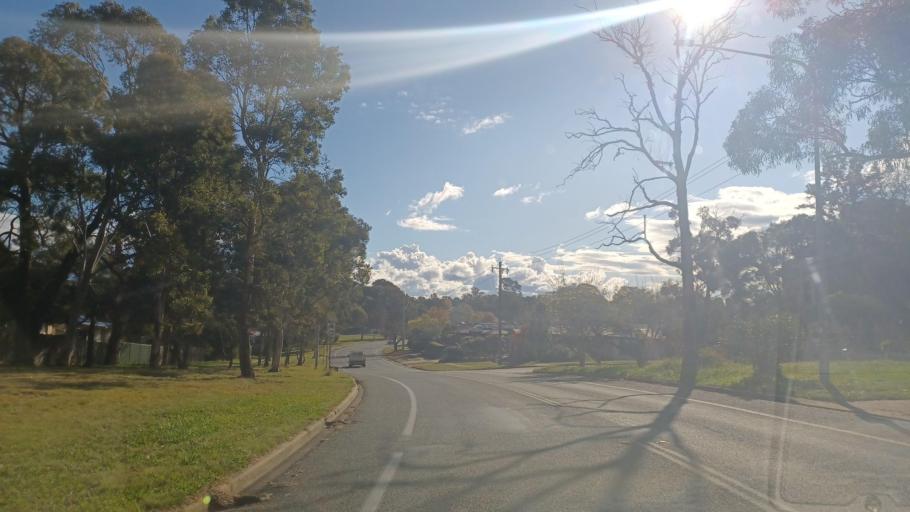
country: AU
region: Australian Capital Territory
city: Belconnen
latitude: -35.1975
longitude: 149.0440
